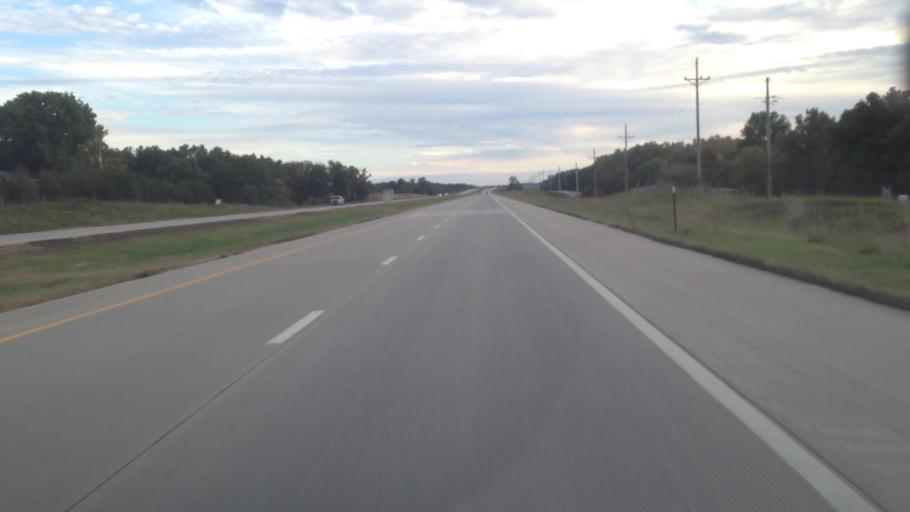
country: US
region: Kansas
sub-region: Douglas County
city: Baldwin City
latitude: 38.7540
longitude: -95.2681
